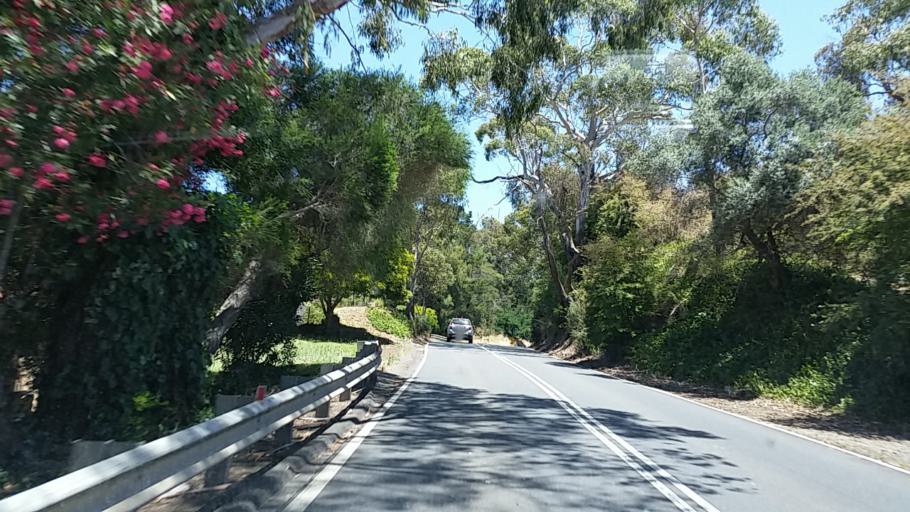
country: AU
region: South Australia
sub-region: Tea Tree Gully
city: Golden Grove
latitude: -34.8248
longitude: 138.7607
